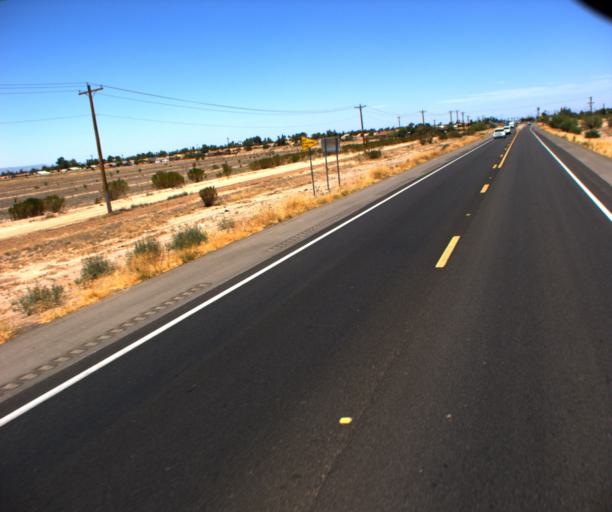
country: US
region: Arizona
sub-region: Maricopa County
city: Sun Lakes
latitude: 33.1981
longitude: -111.8409
